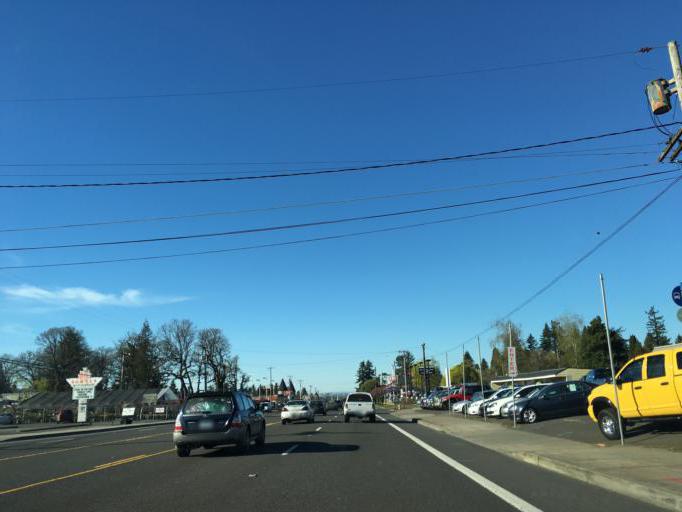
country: US
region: Oregon
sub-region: Clackamas County
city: Oak Grove
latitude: 45.4248
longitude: -122.6337
